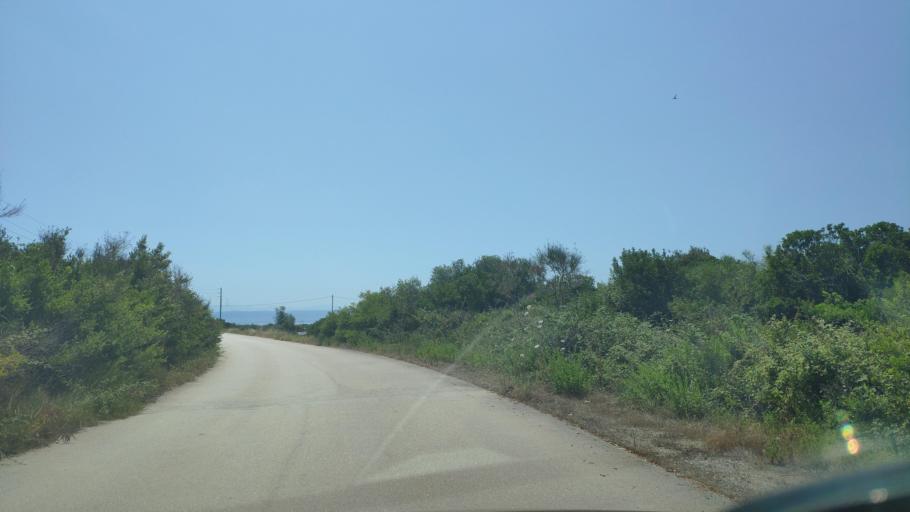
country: GR
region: Epirus
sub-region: Nomos Artas
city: Aneza
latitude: 39.0125
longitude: 20.9234
